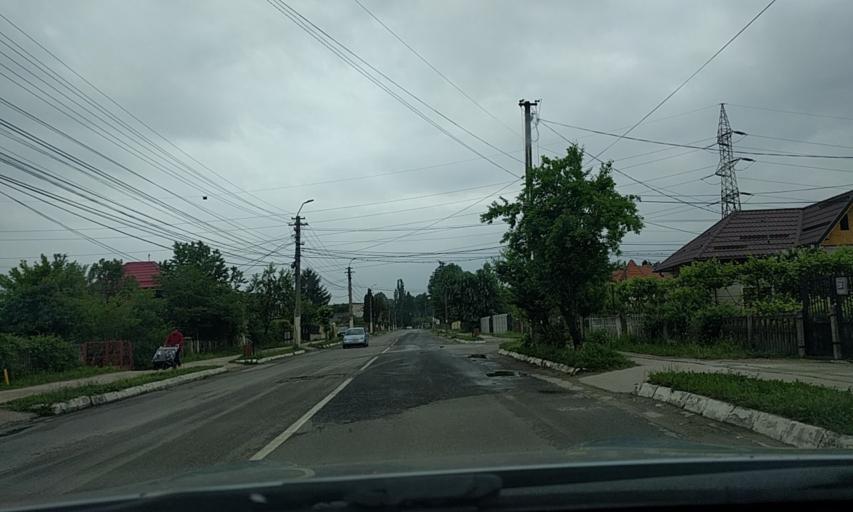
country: RO
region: Dambovita
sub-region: Oras Pucioasa
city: Glodeni
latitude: 45.0562
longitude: 25.4387
